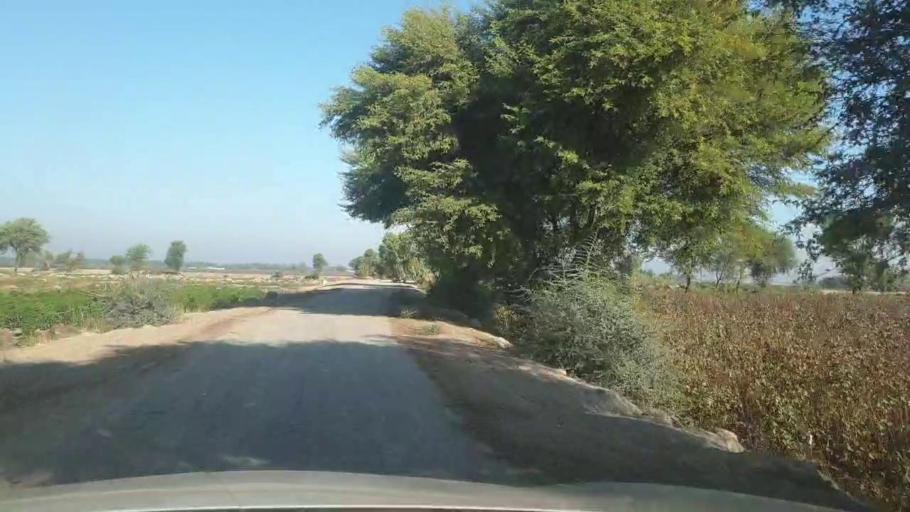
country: PK
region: Sindh
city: Bhan
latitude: 26.5394
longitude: 67.6895
